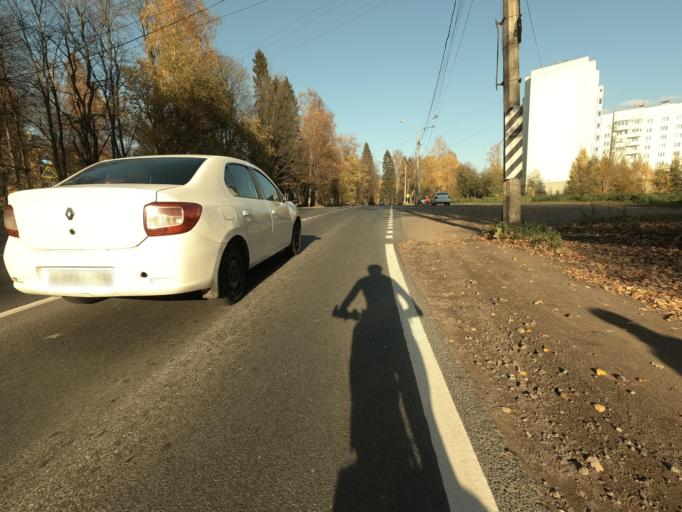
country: RU
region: St.-Petersburg
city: Pargolovo
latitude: 60.1084
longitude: 30.2496
